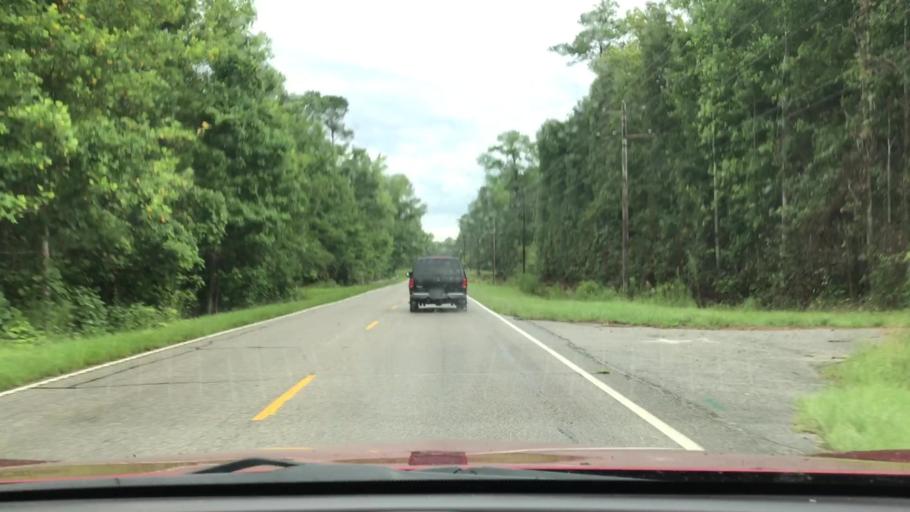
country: US
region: South Carolina
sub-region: Georgetown County
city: Georgetown
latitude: 33.4531
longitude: -79.2800
